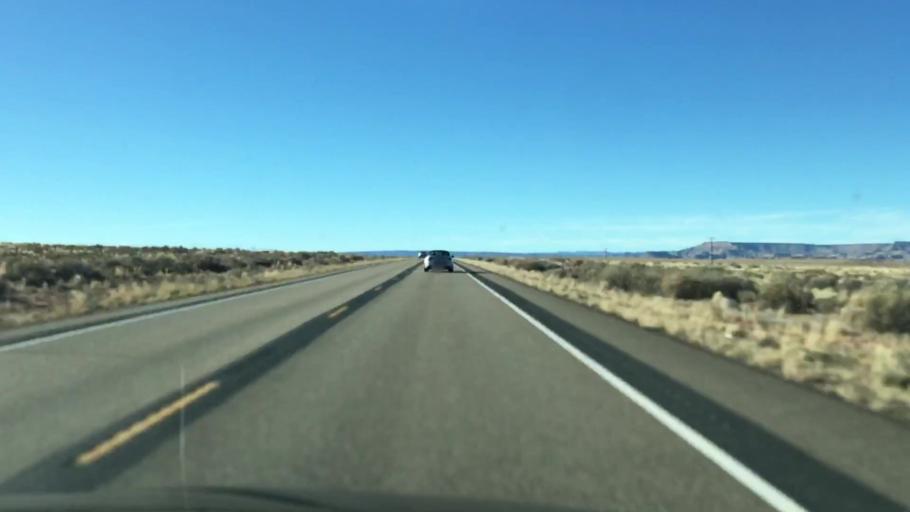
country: US
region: Arizona
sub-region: Coconino County
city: Page
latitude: 37.0899
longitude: -111.7177
